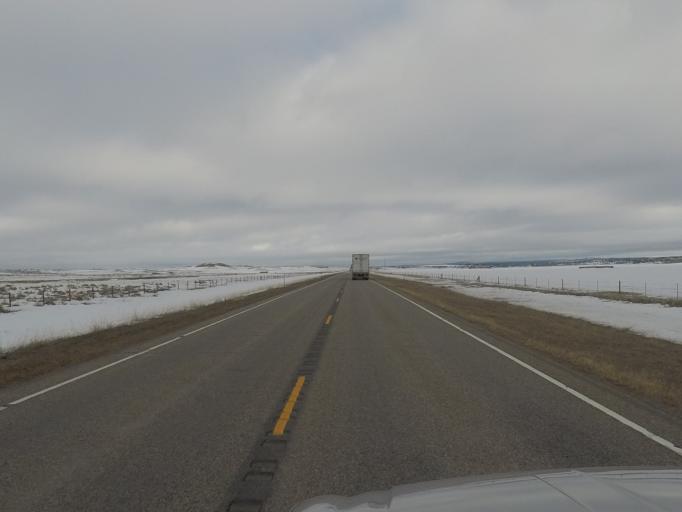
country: US
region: Montana
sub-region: Golden Valley County
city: Ryegate
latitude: 46.3065
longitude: -108.9645
